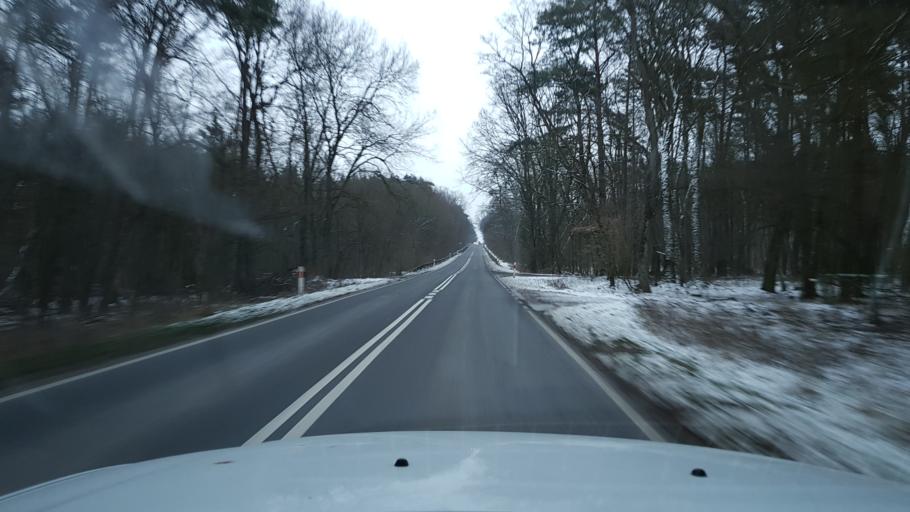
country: PL
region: West Pomeranian Voivodeship
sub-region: Powiat gryfinski
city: Chojna
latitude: 52.9371
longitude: 14.3841
